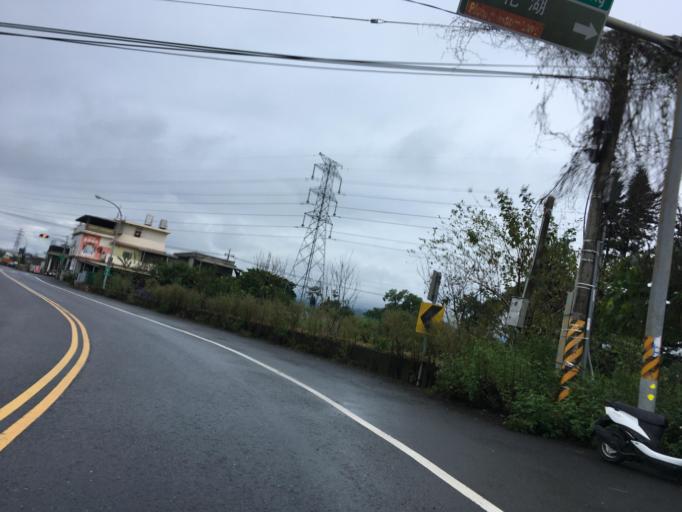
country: TW
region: Taiwan
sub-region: Yilan
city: Yilan
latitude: 24.6645
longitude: 121.7499
